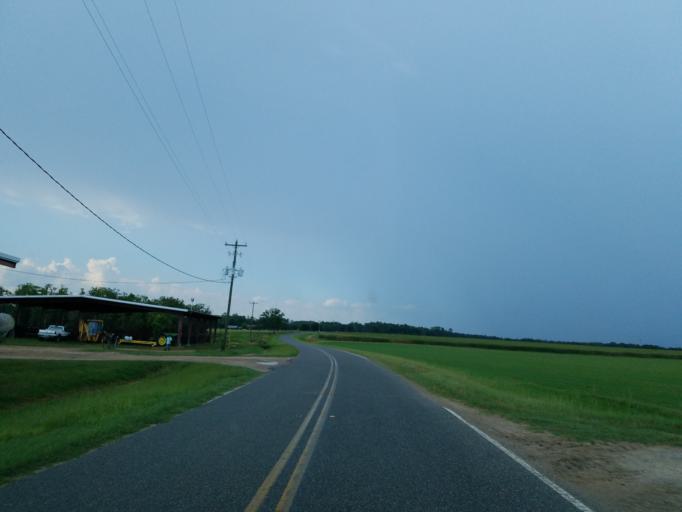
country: US
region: Georgia
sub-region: Cook County
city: Adel
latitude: 31.0799
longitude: -83.4289
